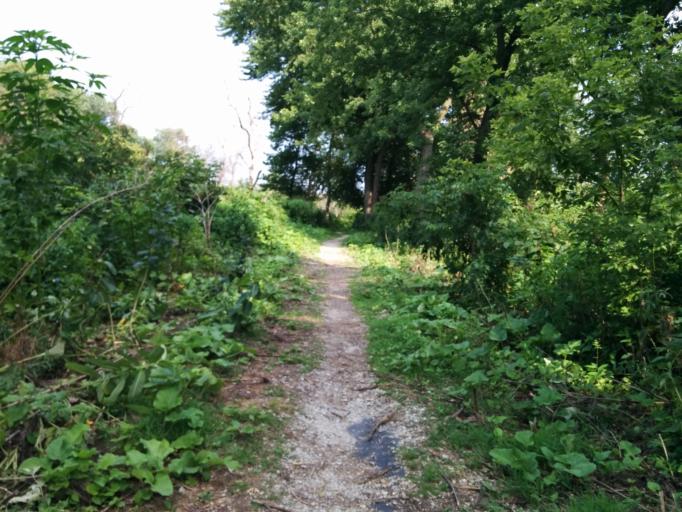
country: US
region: Illinois
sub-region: Cook County
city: Lyons
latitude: 41.8037
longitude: -87.8050
